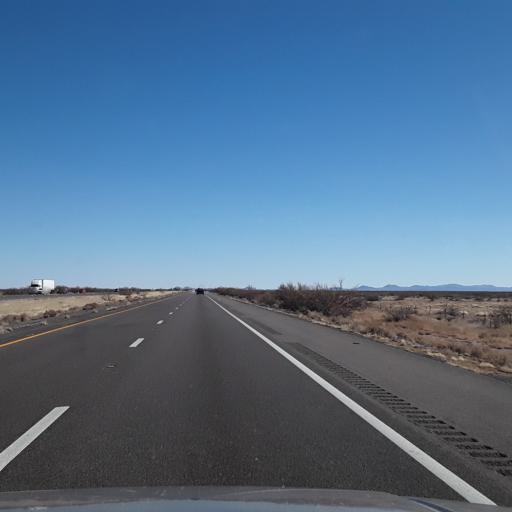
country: US
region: New Mexico
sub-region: Luna County
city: Deming
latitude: 32.2657
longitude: -107.5186
